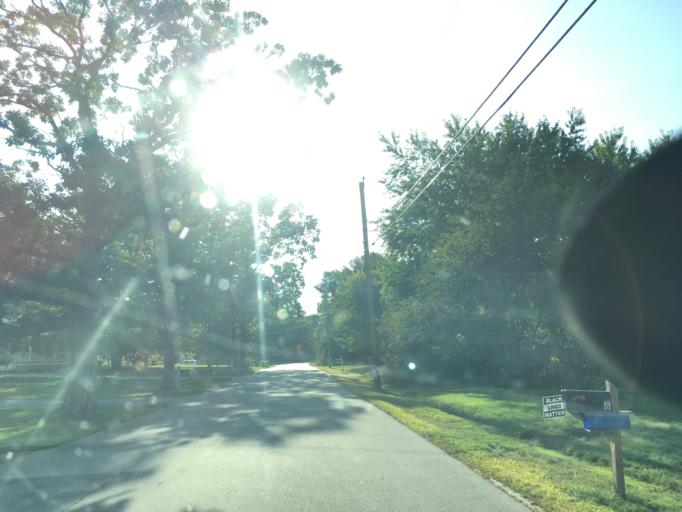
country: US
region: New Hampshire
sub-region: Rockingham County
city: Exeter
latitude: 42.9707
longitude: -70.9500
